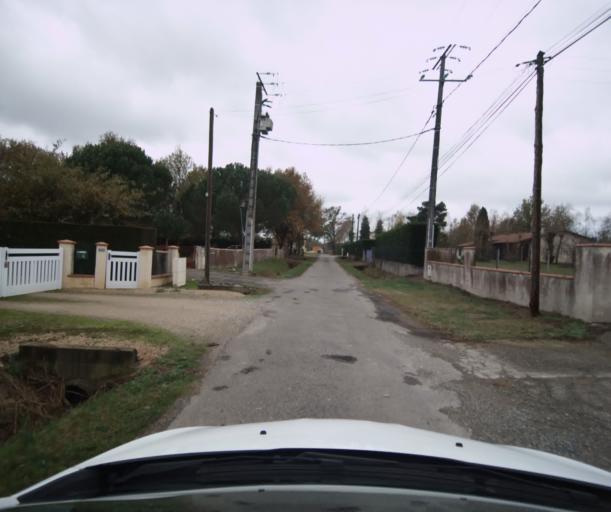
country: FR
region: Midi-Pyrenees
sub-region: Departement du Tarn-et-Garonne
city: Saint-Porquier
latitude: 44.0498
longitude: 1.1712
